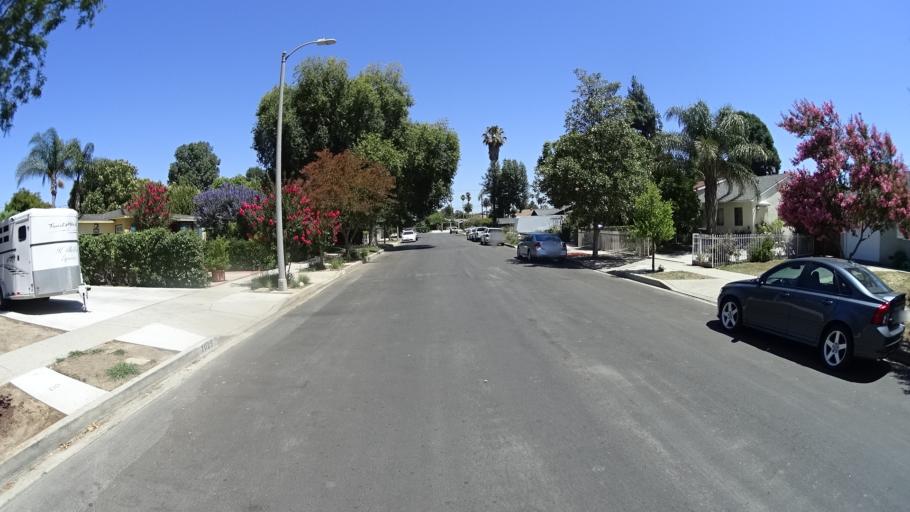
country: US
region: California
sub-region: Los Angeles County
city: Northridge
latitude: 34.1982
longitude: -118.5295
